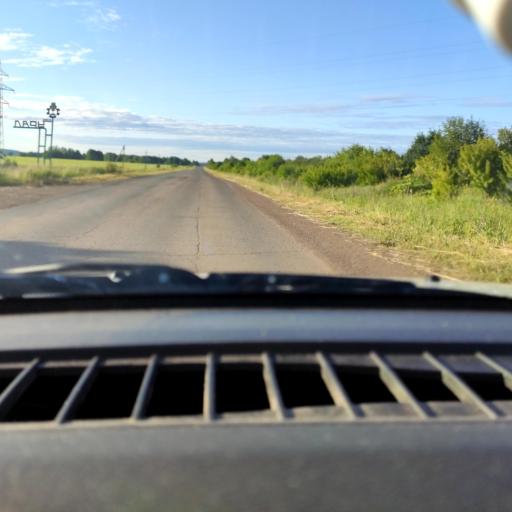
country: RU
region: Perm
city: Uinskoye
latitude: 57.1049
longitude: 56.5349
